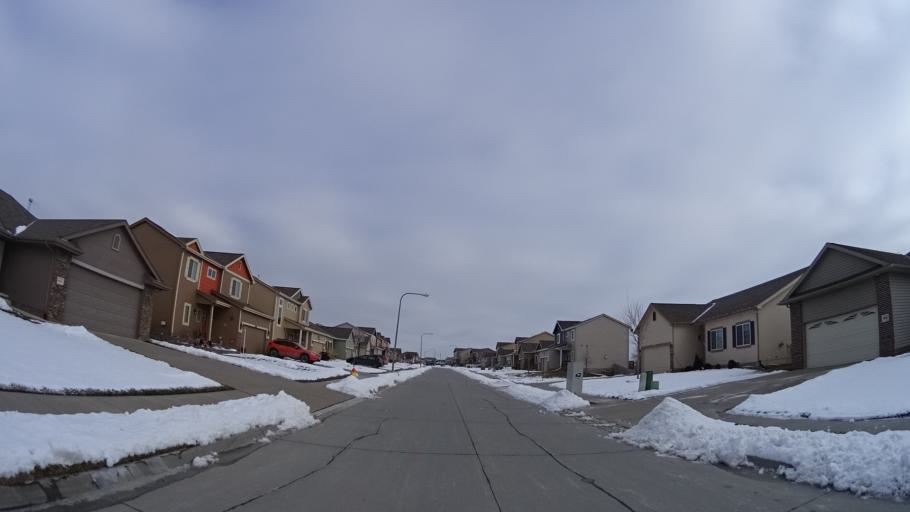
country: US
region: Nebraska
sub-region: Sarpy County
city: Offutt Air Force Base
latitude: 41.1040
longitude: -95.9839
